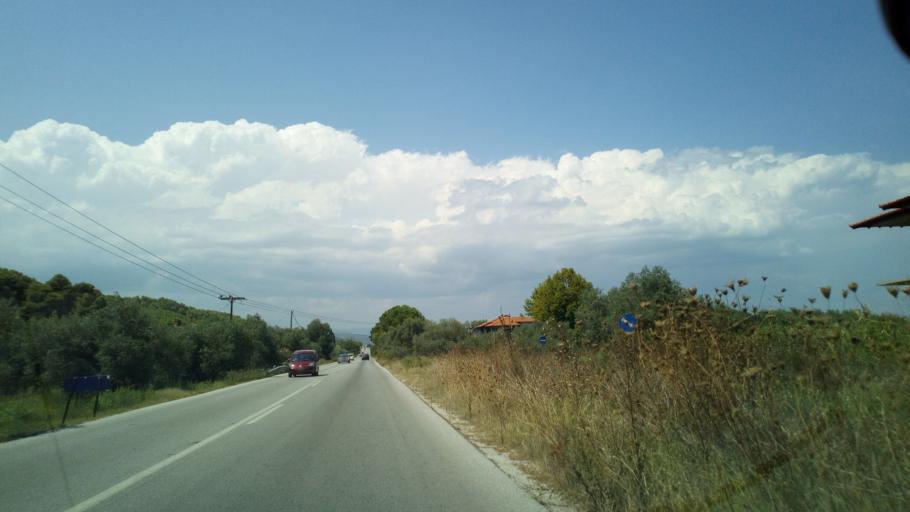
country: GR
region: Central Macedonia
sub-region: Nomos Chalkidikis
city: Agios Nikolaos
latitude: 40.2182
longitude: 23.7511
